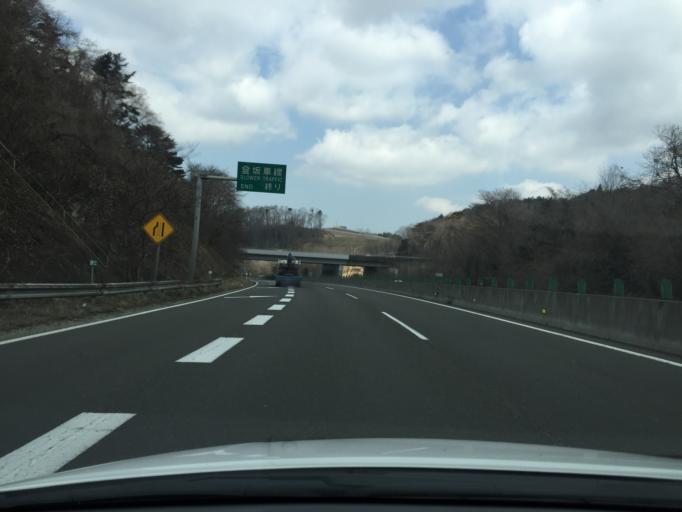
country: JP
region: Miyagi
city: Sendai
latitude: 38.2493
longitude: 140.8174
